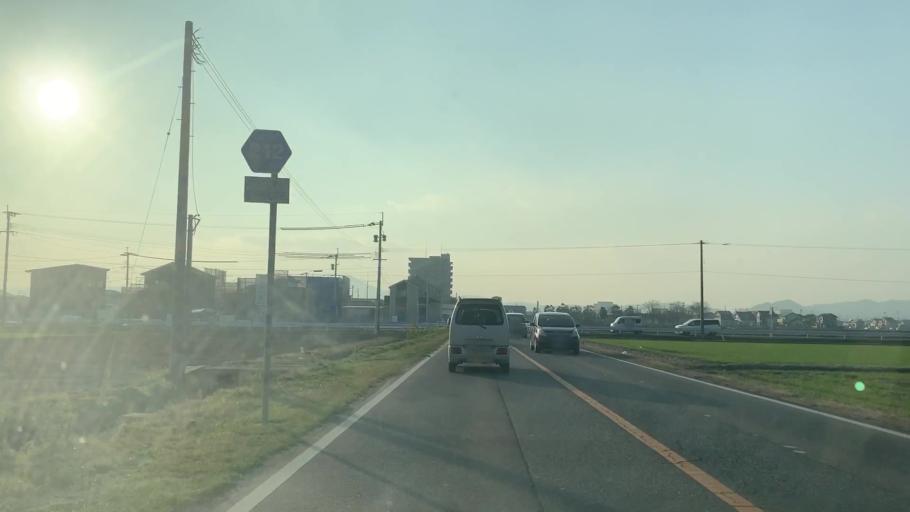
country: JP
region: Saga Prefecture
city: Saga-shi
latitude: 33.2784
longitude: 130.2222
